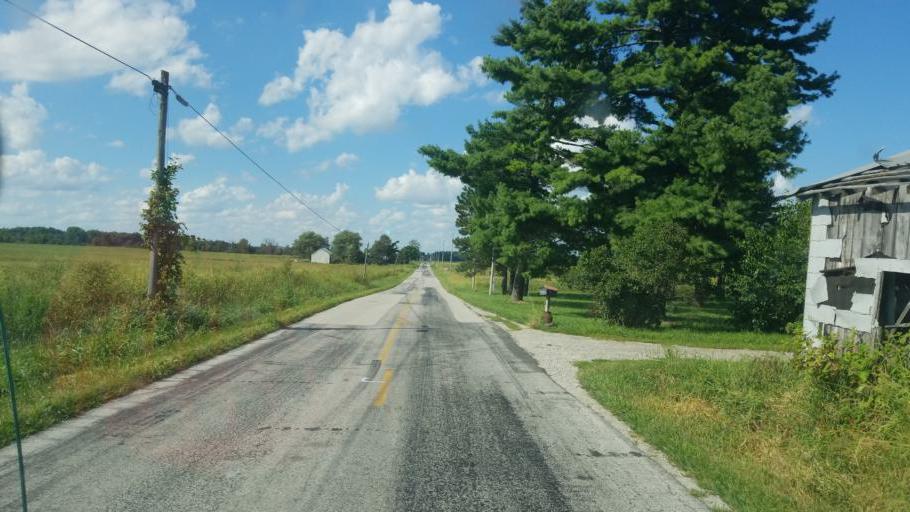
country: US
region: Ohio
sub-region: Union County
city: Richwood
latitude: 40.5162
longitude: -83.3840
